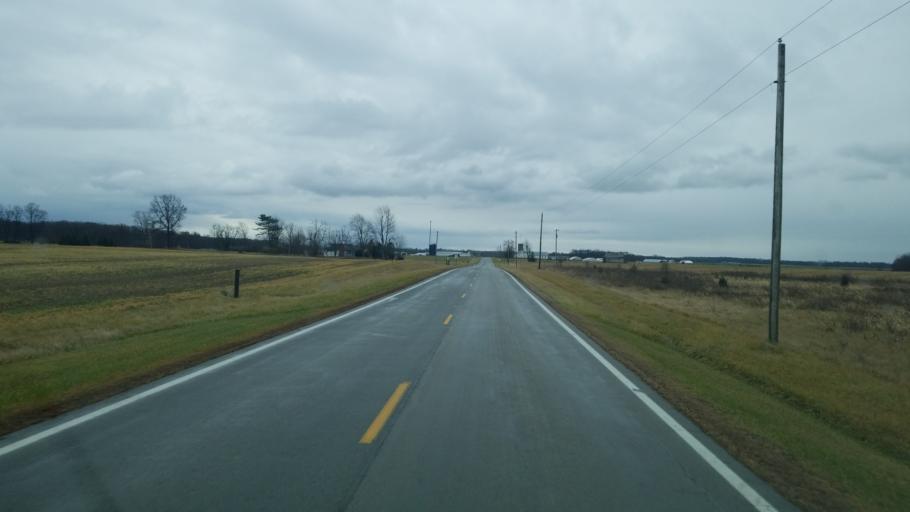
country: US
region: Ohio
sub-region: Hardin County
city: Forest
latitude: 40.7179
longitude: -83.4132
